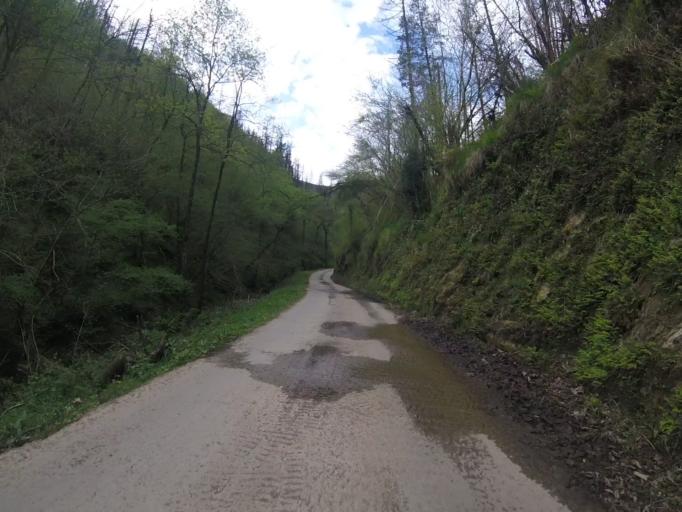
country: ES
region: Basque Country
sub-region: Provincia de Guipuzcoa
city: Errezil
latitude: 43.2053
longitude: -2.1829
